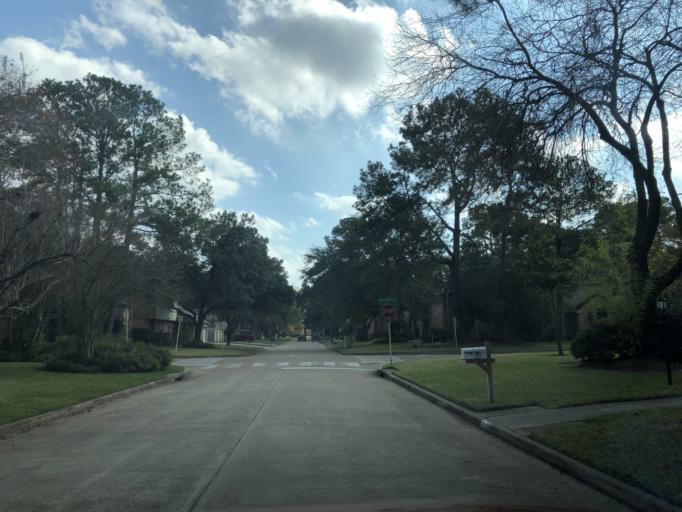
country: US
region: Texas
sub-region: Harris County
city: Tomball
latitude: 30.0236
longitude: -95.5427
